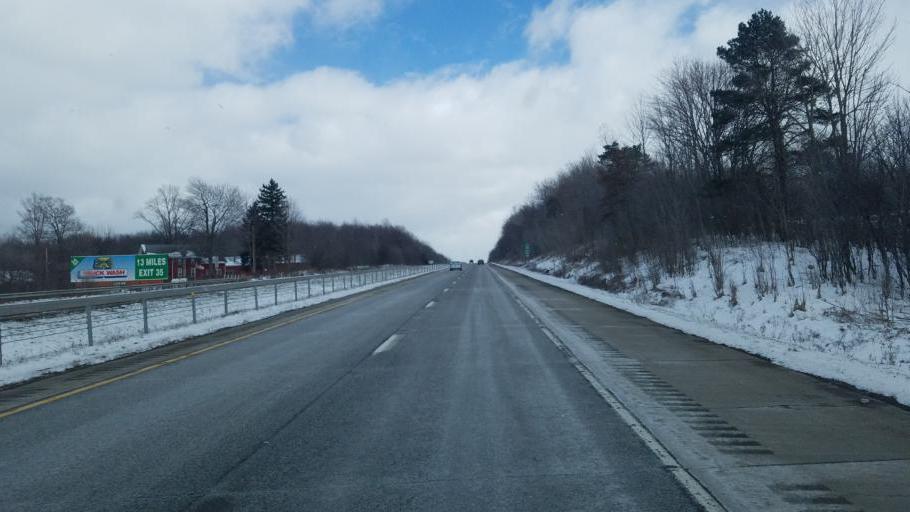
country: US
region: Pennsylvania
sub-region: Erie County
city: Fairview
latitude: 42.0219
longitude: -80.1587
